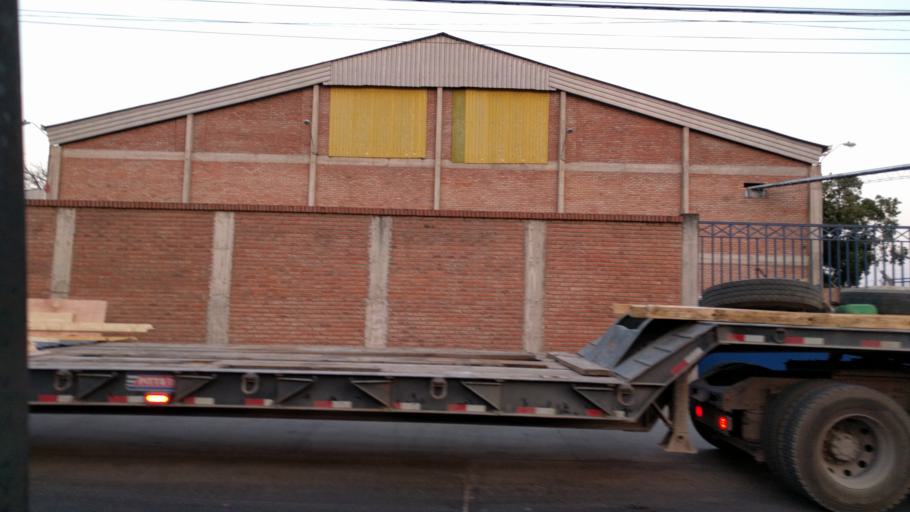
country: BO
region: Santa Cruz
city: Santa Cruz de la Sierra
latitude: -17.7612
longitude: -63.1461
